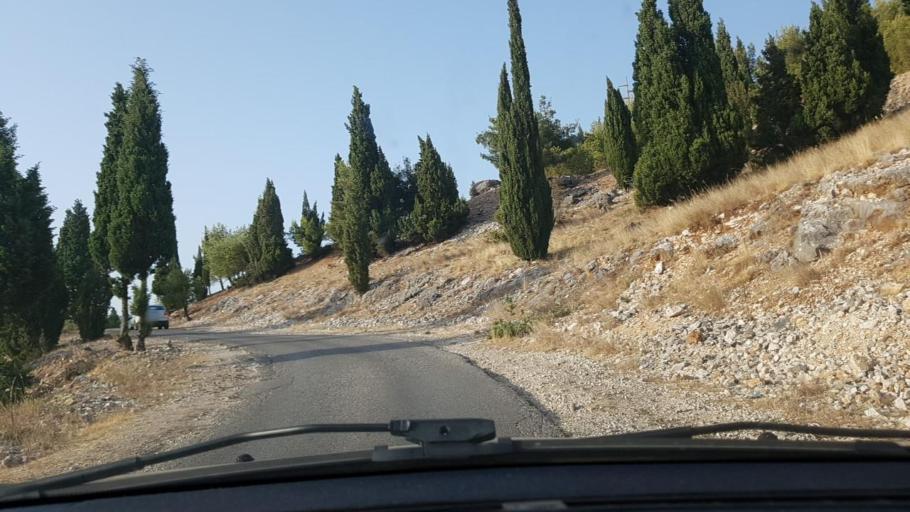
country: BA
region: Federation of Bosnia and Herzegovina
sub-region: Hercegovacko-Bosanski Kanton
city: Mostar
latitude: 43.3508
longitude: 17.8228
